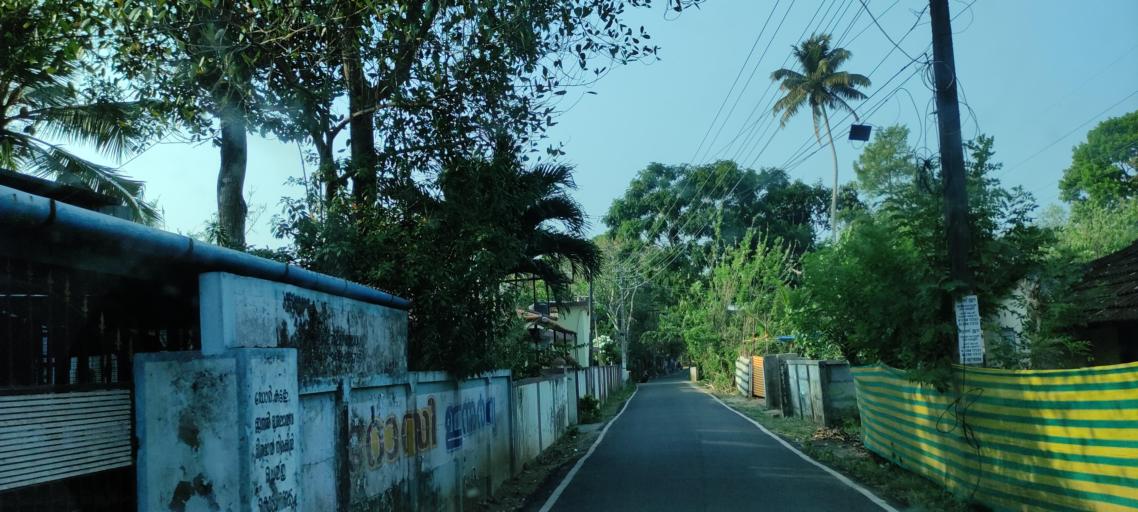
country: IN
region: Kerala
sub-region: Alappuzha
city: Alleppey
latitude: 9.5169
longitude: 76.3222
